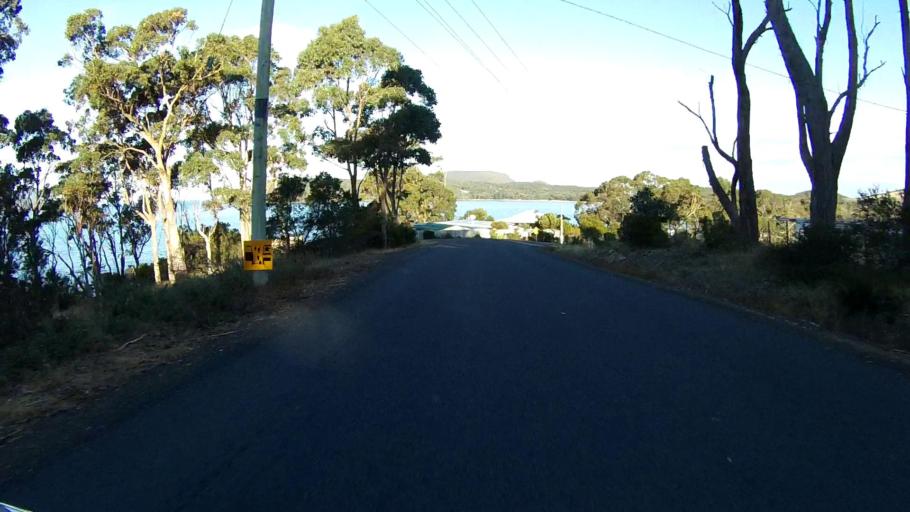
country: AU
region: Tasmania
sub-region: Clarence
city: Sandford
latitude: -43.1732
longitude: 147.8548
